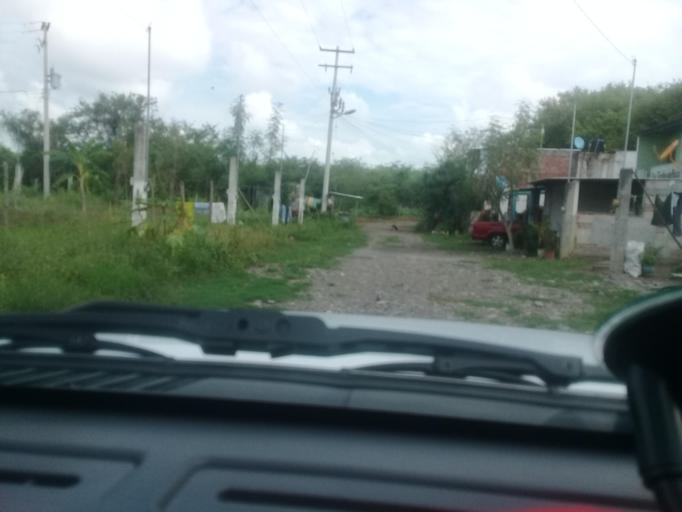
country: MX
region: Veracruz
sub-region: Paso de Ovejas
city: Tolome
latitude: 19.2713
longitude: -96.4190
